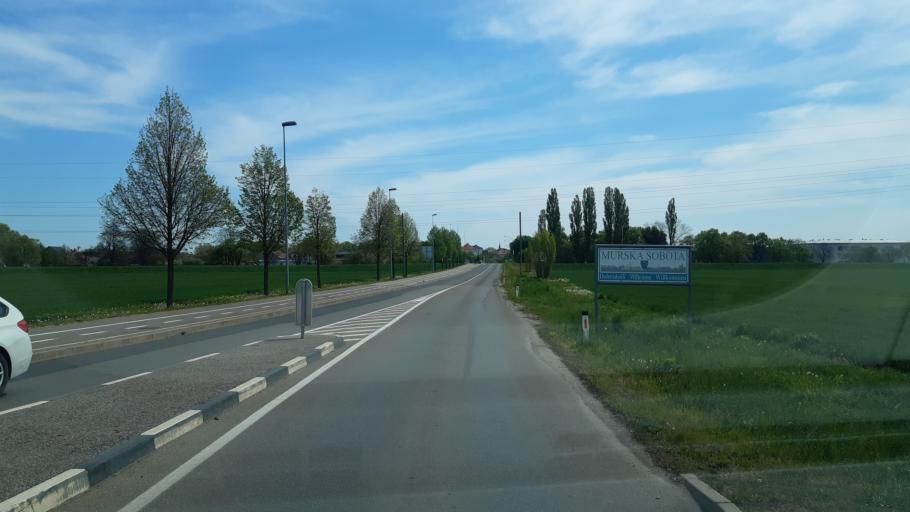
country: SI
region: Murska Sobota
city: Cernelavci
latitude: 46.6623
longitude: 16.1472
